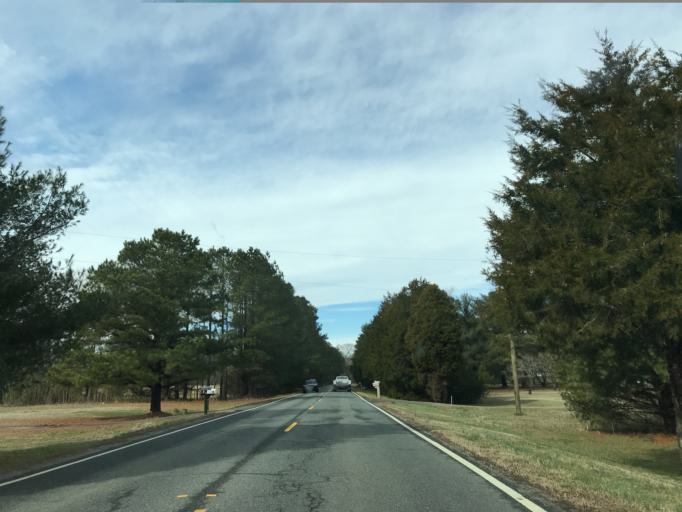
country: US
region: Virginia
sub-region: King George County
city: Dahlgren
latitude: 38.2854
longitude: -77.0511
